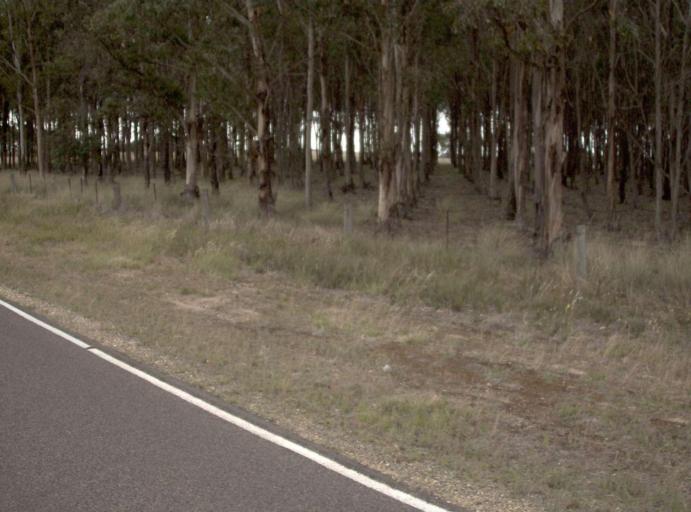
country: AU
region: Victoria
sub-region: East Gippsland
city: Bairnsdale
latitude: -37.9673
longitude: 147.4814
